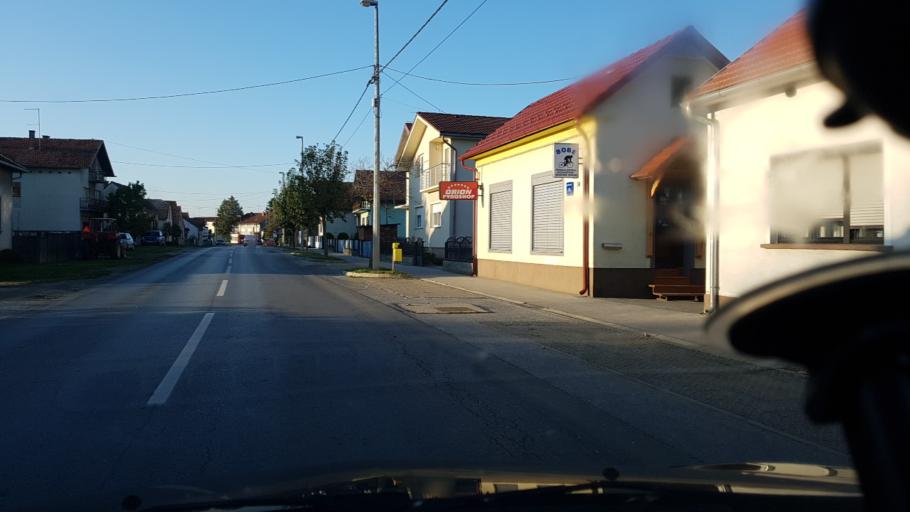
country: HR
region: Koprivnicko-Krizevacka
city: Kalinovac
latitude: 46.0437
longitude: 17.0576
